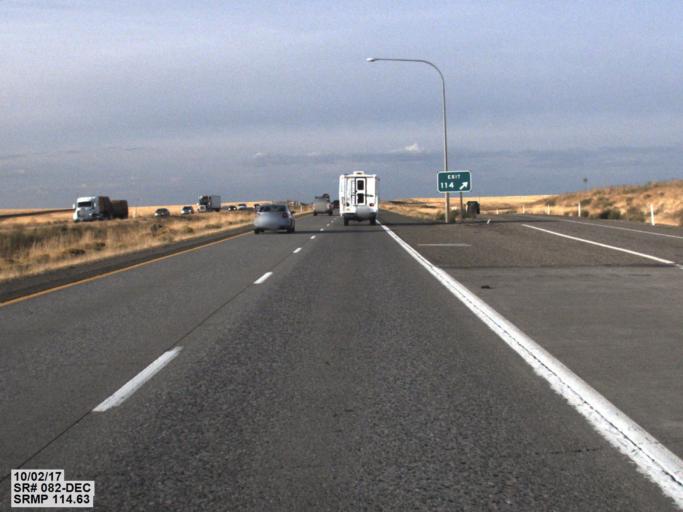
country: US
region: Washington
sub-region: Benton County
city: Highland
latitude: 46.1390
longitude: -119.2019
